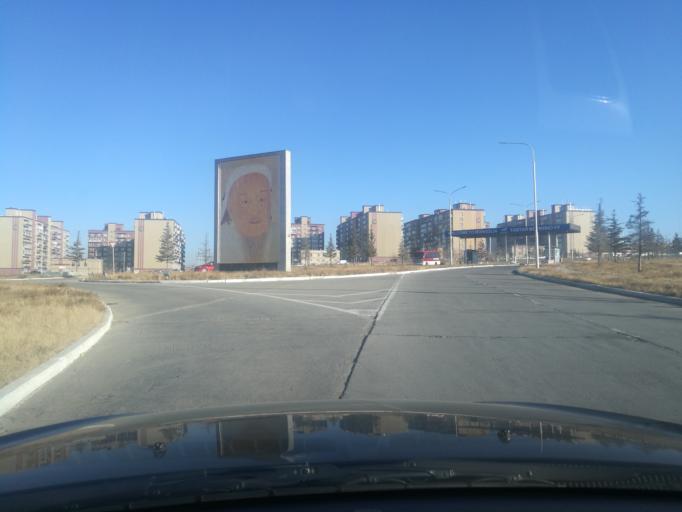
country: MN
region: Ulaanbaatar
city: Ulaanbaatar
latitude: 47.8540
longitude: 106.7653
